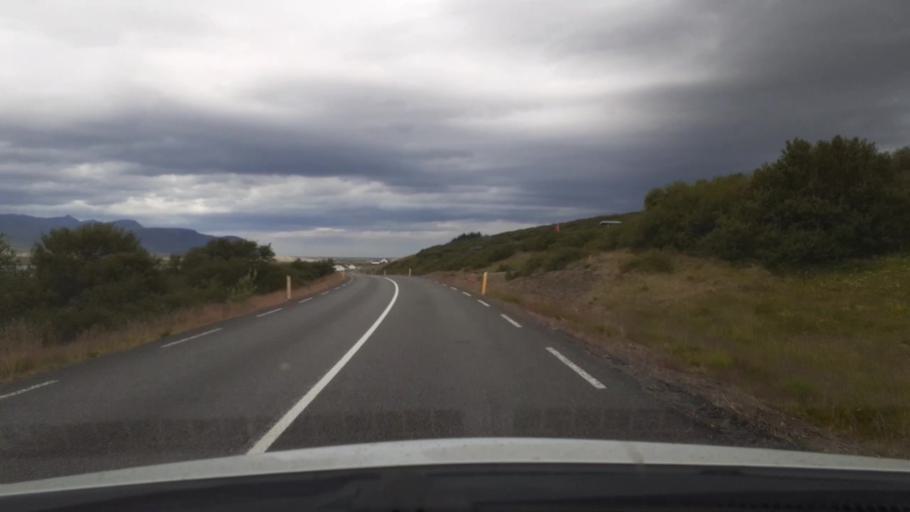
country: IS
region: West
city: Borgarnes
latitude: 64.5429
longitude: -21.5616
